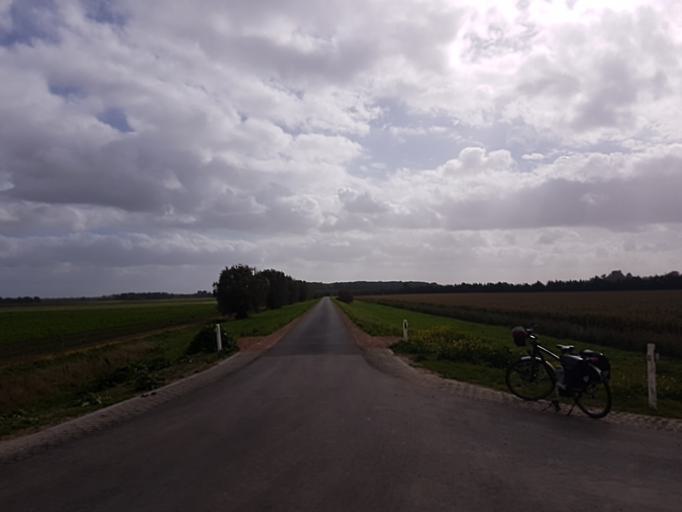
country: NL
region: South Holland
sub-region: Gemeente Dordrecht
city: Dordrecht
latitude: 51.7623
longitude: 4.6606
